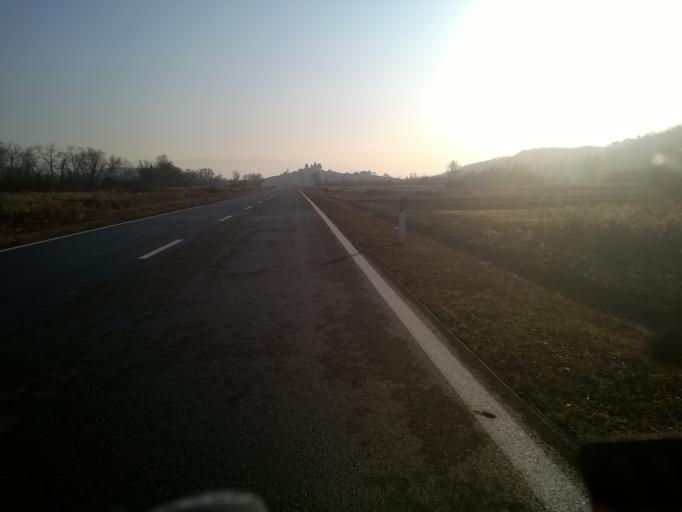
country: HR
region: Krapinsko-Zagorska
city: Zabok
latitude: 46.0512
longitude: 15.9131
